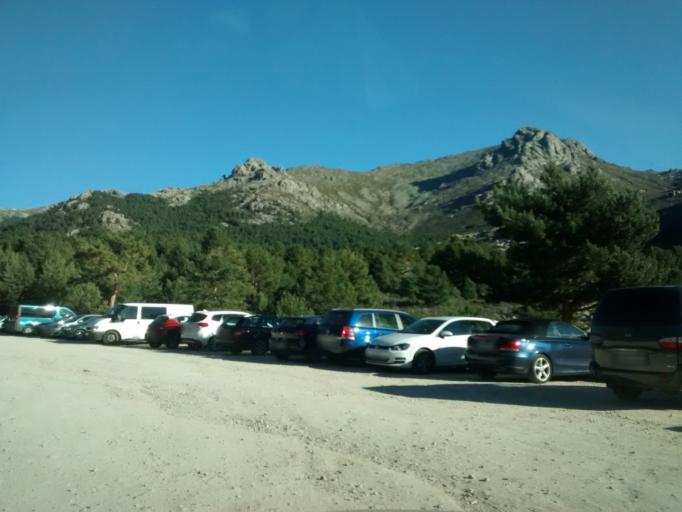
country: ES
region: Madrid
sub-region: Provincia de Madrid
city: Navacerrada
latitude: 40.7520
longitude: -3.9930
